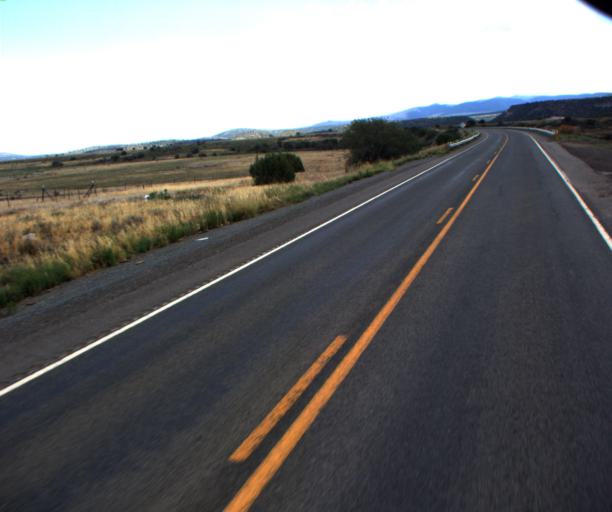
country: US
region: Arizona
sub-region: Yavapai County
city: Camp Verde
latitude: 34.5158
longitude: -112.0225
